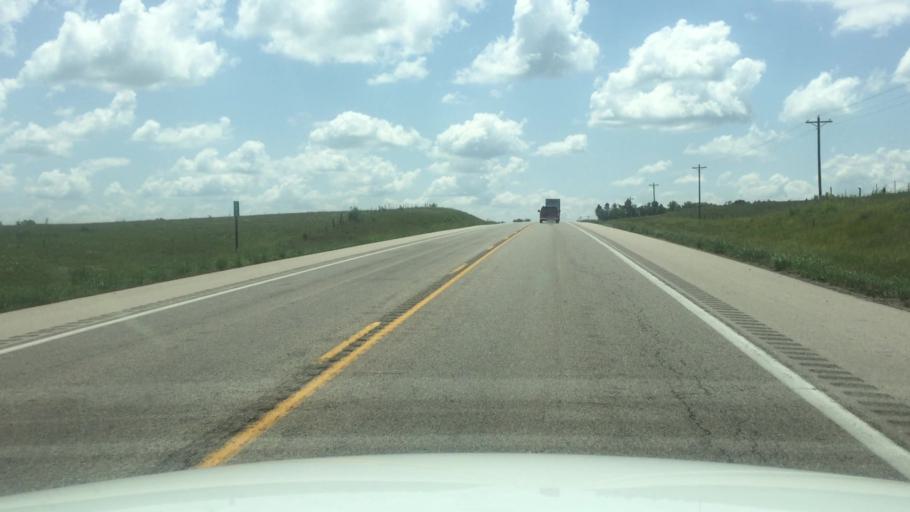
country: US
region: Kansas
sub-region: Brown County
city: Horton
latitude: 39.6795
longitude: -95.7306
